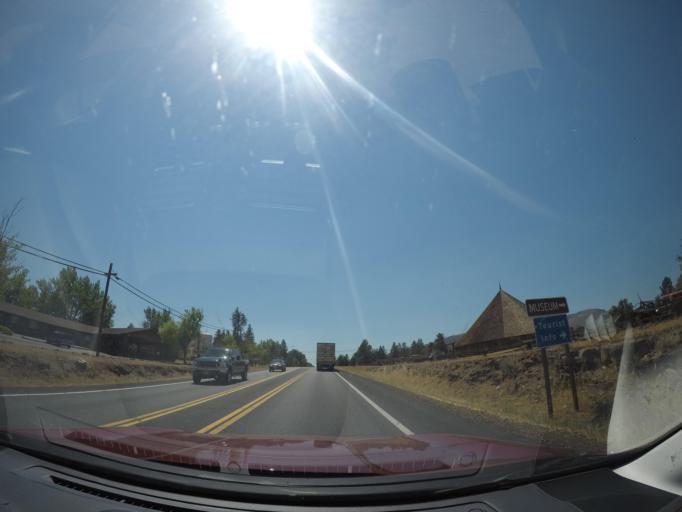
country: US
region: California
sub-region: Shasta County
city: Burney
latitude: 41.0017
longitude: -121.4453
